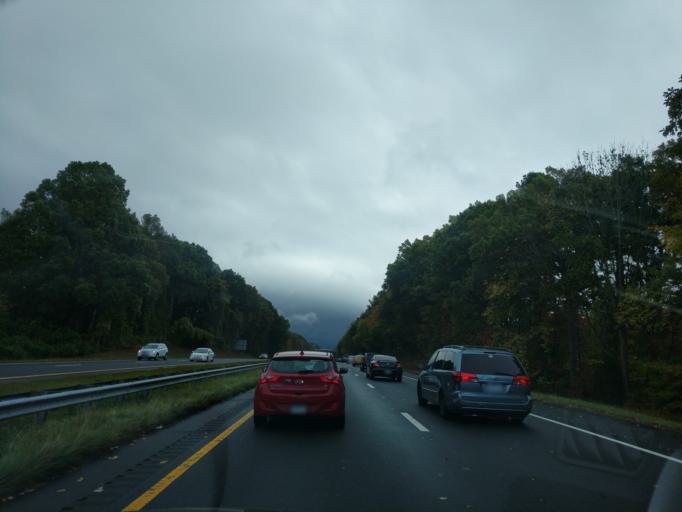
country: US
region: North Carolina
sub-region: Orange County
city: Hillsborough
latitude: 36.0568
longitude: -79.0757
